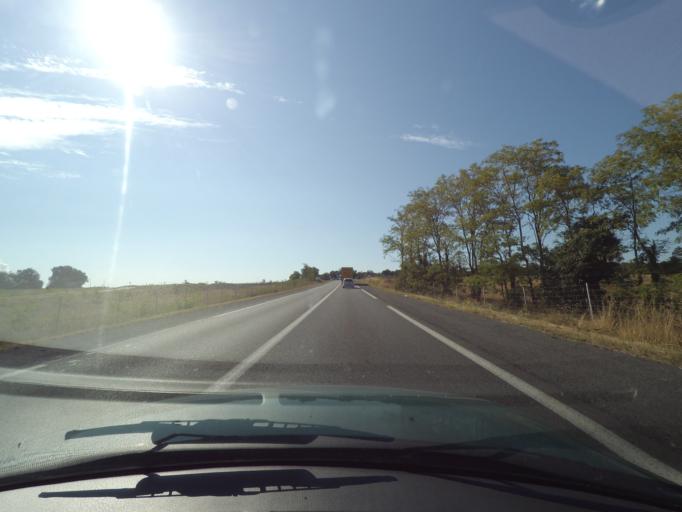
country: FR
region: Poitou-Charentes
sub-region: Departement de la Vienne
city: Terce
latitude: 46.4580
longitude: 0.5556
